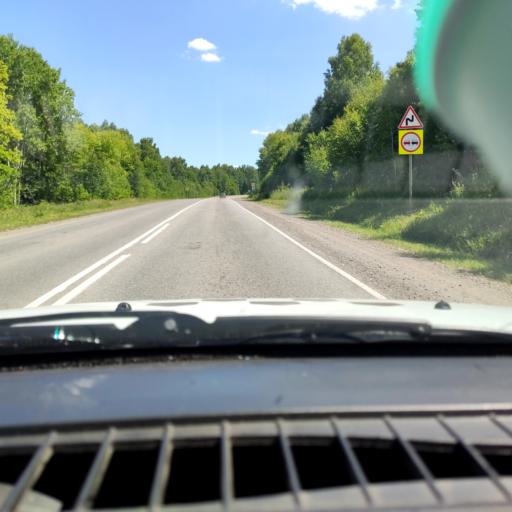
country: RU
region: Bashkortostan
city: Verkhniye Kigi
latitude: 55.3855
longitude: 58.6709
